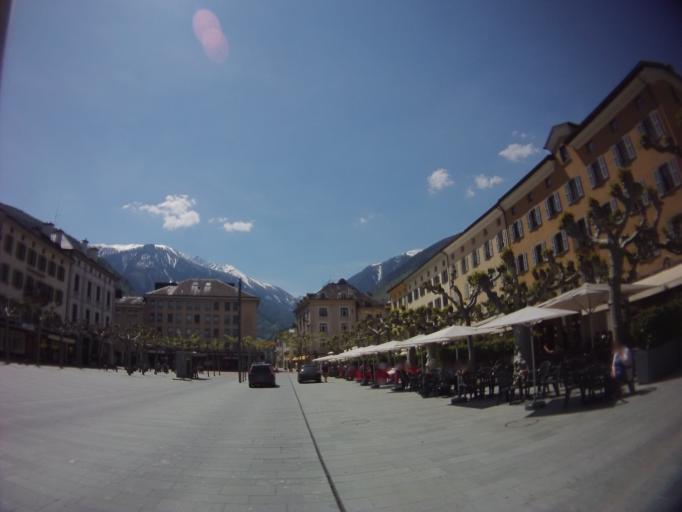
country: CH
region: Valais
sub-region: Martigny District
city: Martigny-Ville
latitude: 46.1015
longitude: 7.0731
